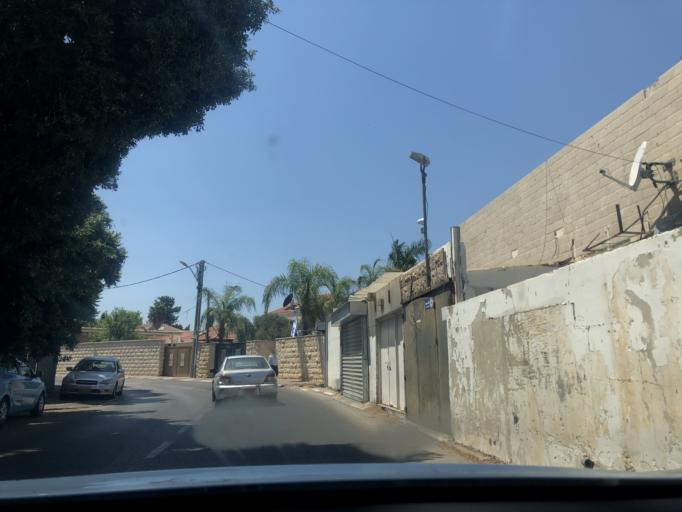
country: IL
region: Central District
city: Lod
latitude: 31.9390
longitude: 34.8862
